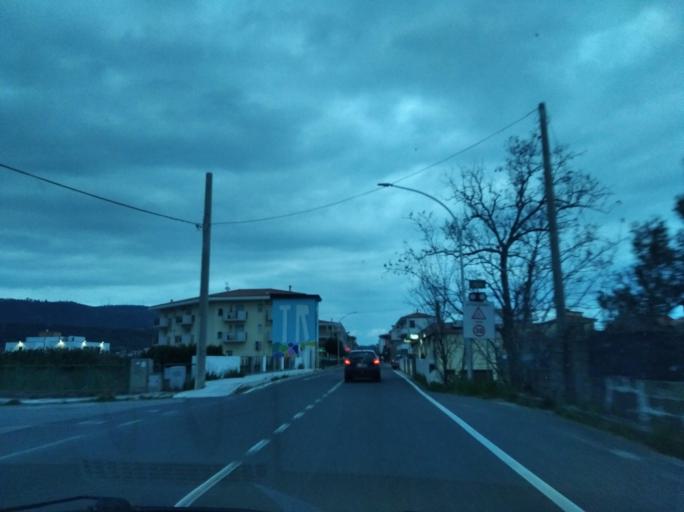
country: IT
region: Calabria
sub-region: Provincia di Catanzaro
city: Montepaone Lido
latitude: 38.7250
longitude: 16.5380
